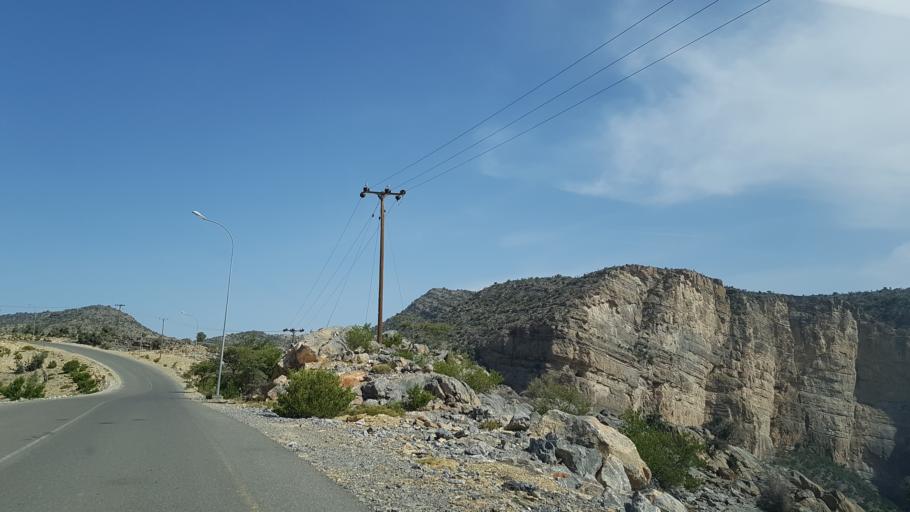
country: OM
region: Al Batinah
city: Bayt al `Awabi
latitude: 23.1363
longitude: 57.5565
